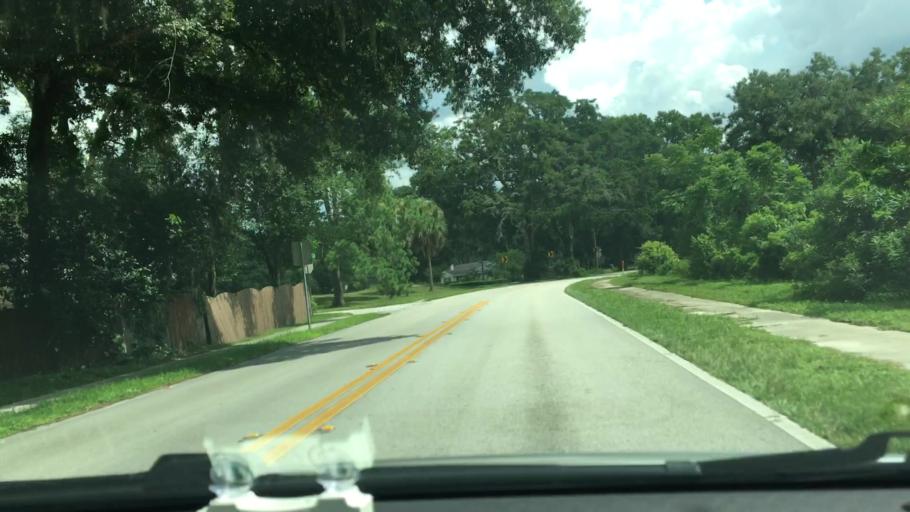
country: US
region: Florida
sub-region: Seminole County
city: Altamonte Springs
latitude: 28.6898
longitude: -81.3712
